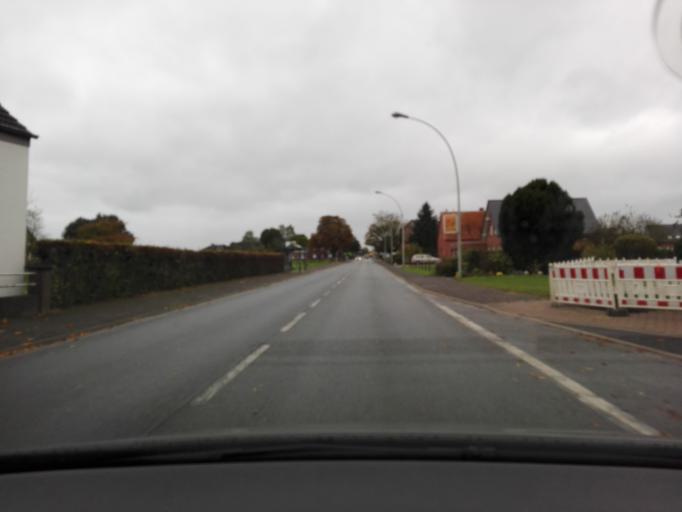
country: DE
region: North Rhine-Westphalia
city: Selm
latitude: 51.6643
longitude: 7.4855
